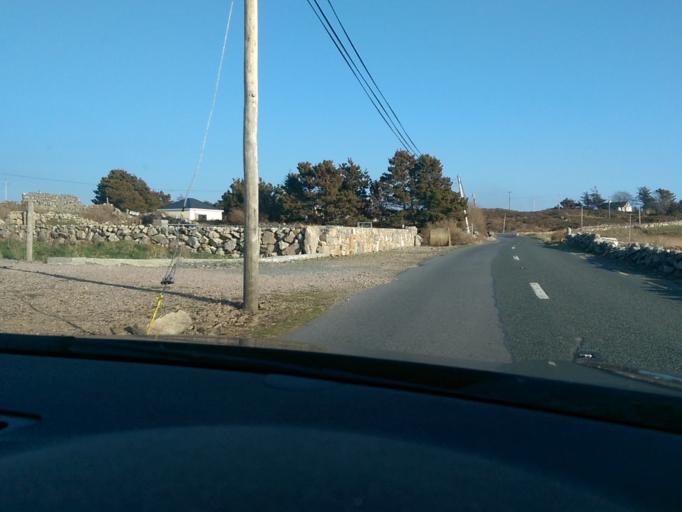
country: IE
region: Connaught
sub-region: County Galway
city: Clifden
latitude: 53.3185
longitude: -9.8067
